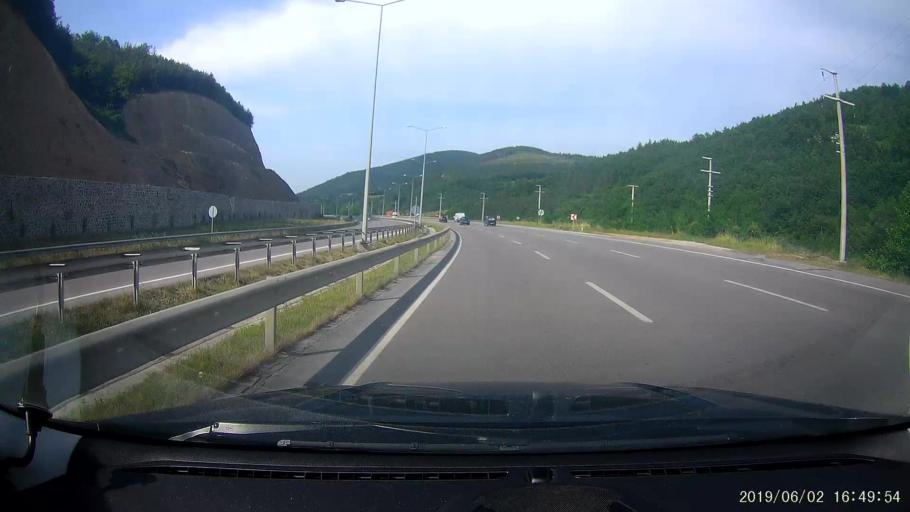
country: TR
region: Samsun
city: Samsun
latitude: 41.2439
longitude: 36.1709
